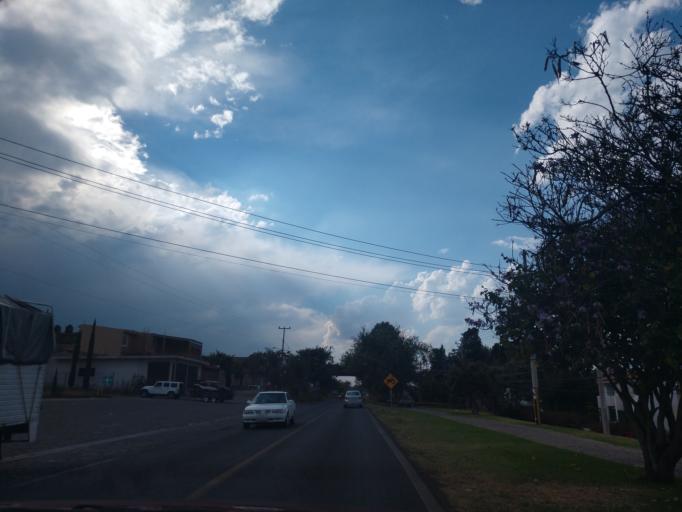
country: MX
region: Jalisco
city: San Juan Cosala
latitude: 20.2019
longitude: -103.3119
